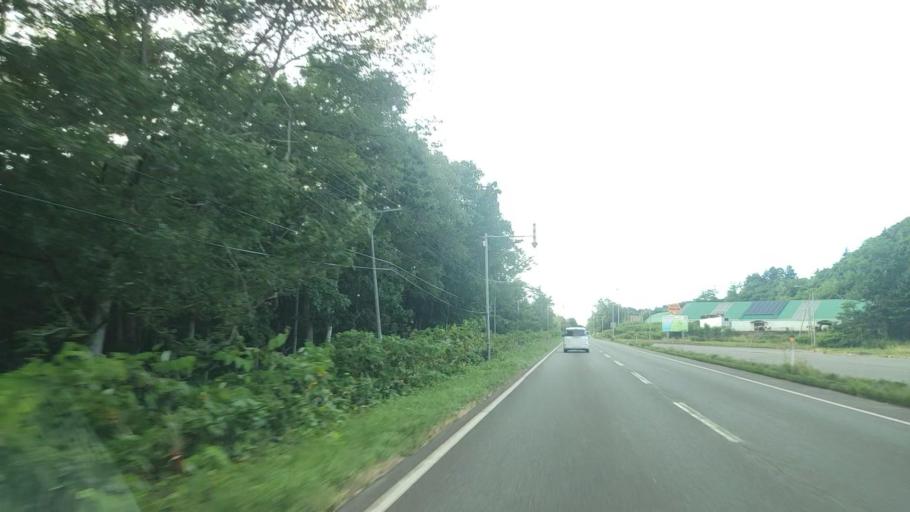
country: JP
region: Hokkaido
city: Makubetsu
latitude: 45.0432
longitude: 141.7550
